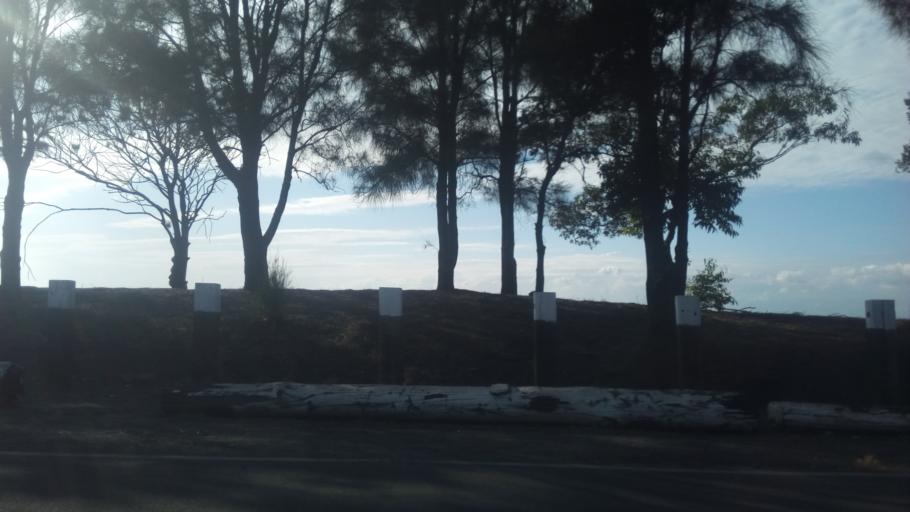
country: AU
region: New South Wales
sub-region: Wollongong
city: Port Kembla
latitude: -34.4657
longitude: 150.8997
